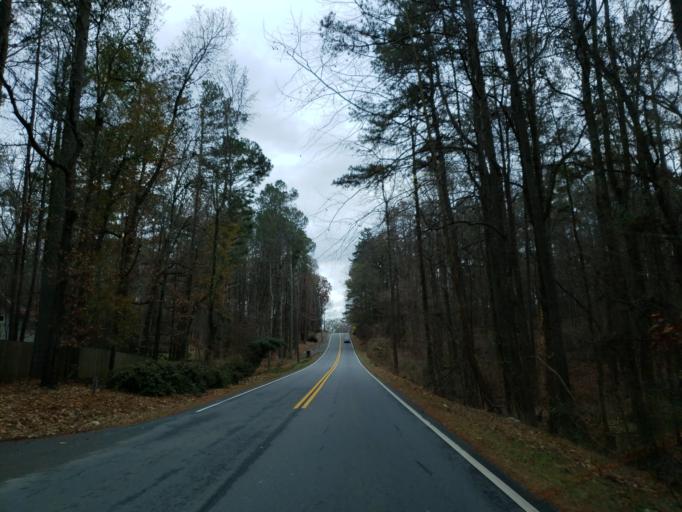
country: US
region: Georgia
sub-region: Cobb County
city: Fair Oaks
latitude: 33.9155
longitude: -84.5971
